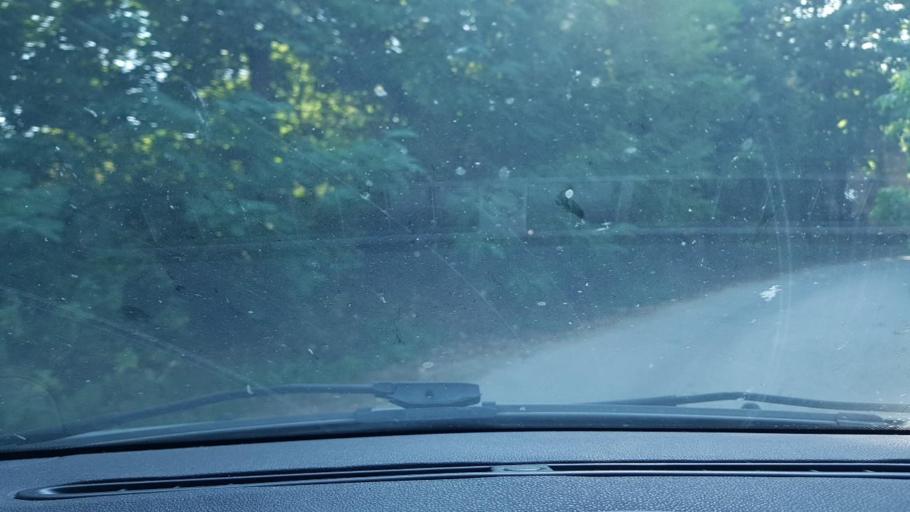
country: BA
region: Federation of Bosnia and Herzegovina
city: Ostrozac
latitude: 44.9074
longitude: 15.9365
